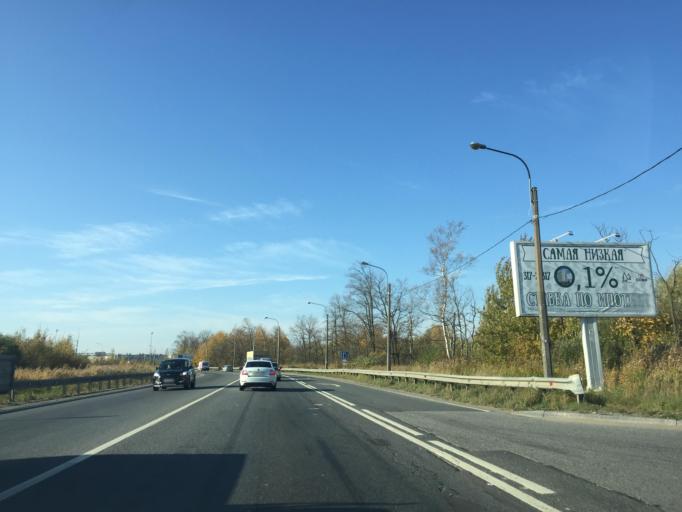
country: RU
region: St.-Petersburg
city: Petro-Slavyanka
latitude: 59.7474
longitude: 30.5074
